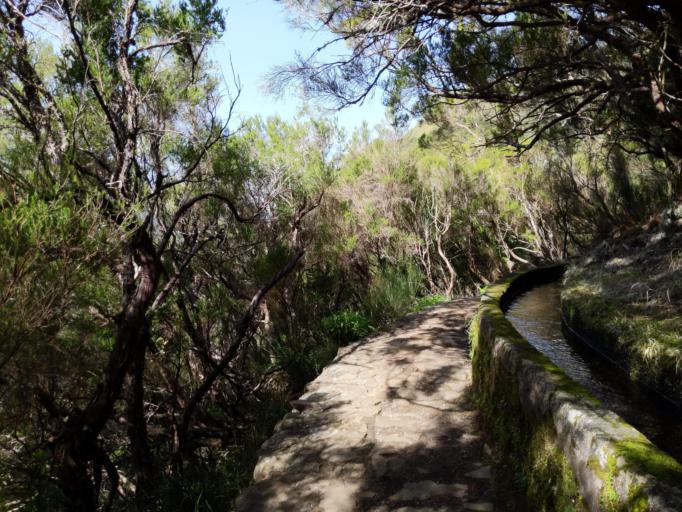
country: PT
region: Madeira
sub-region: Calheta
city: Arco da Calheta
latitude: 32.7625
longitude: -17.1260
